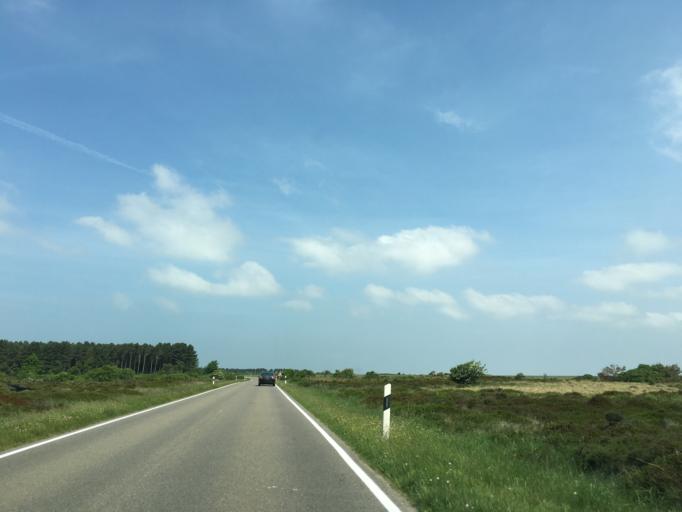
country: DE
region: Schleswig-Holstein
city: Nebel
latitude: 54.6593
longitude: 8.3426
